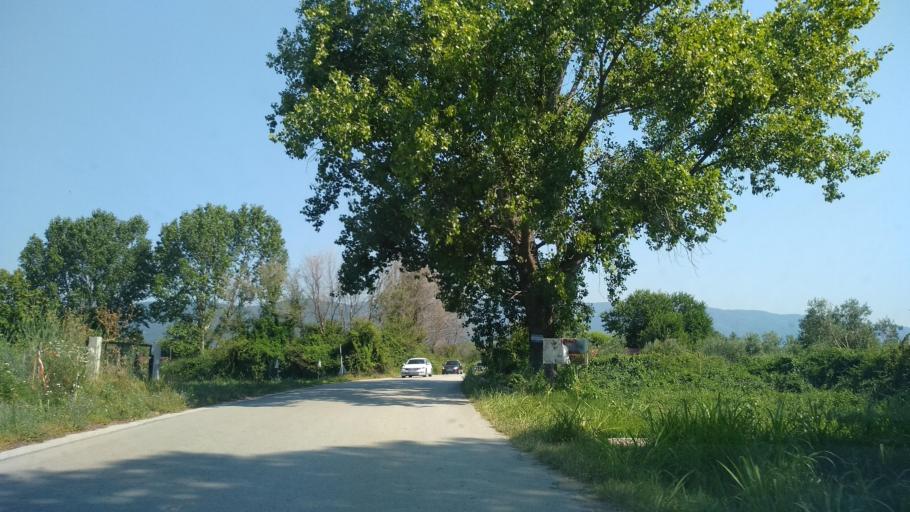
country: GR
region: Central Macedonia
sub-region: Nomos Thessalonikis
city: Stavros
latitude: 40.6757
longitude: 23.6880
